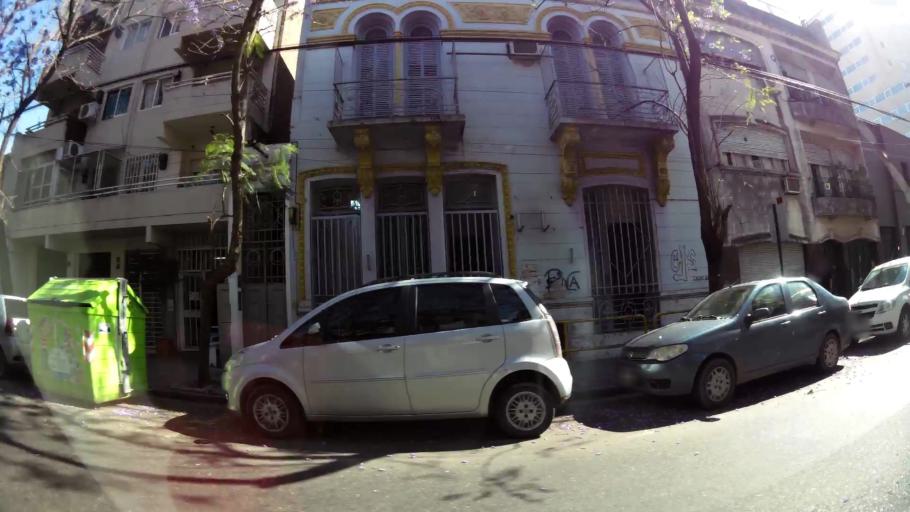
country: AR
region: Santa Fe
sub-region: Departamento de Rosario
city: Rosario
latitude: -32.9481
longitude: -60.6507
